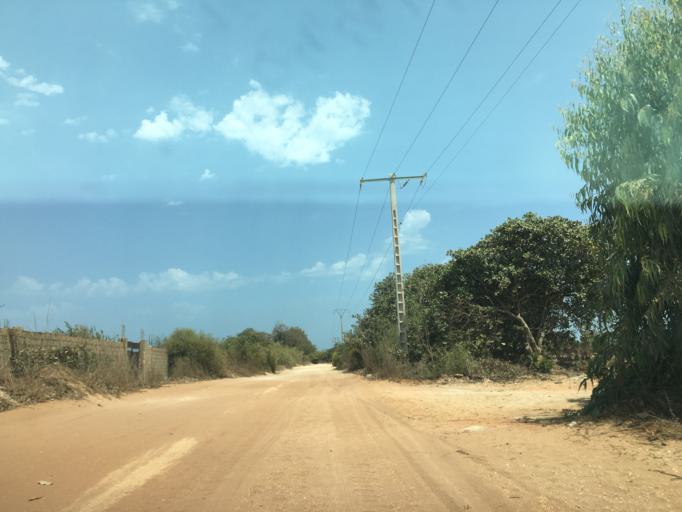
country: SN
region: Thies
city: Thies
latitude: 14.8158
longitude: -17.1954
